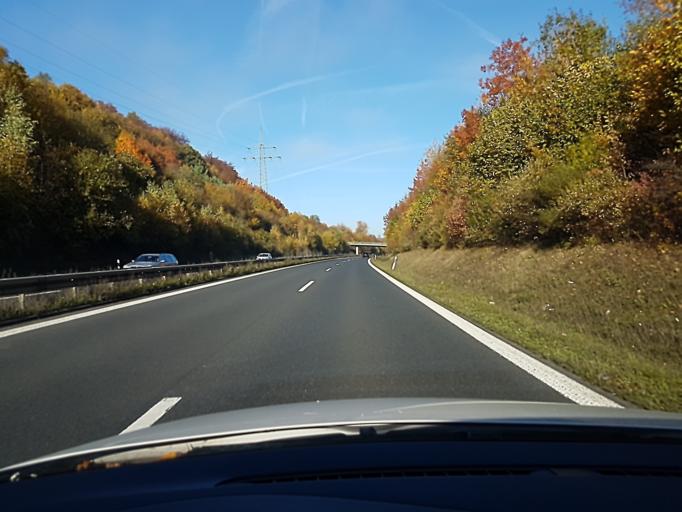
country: DE
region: Bavaria
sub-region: Regierungsbezirk Unterfranken
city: Worth am Main
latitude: 49.7863
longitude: 9.1495
